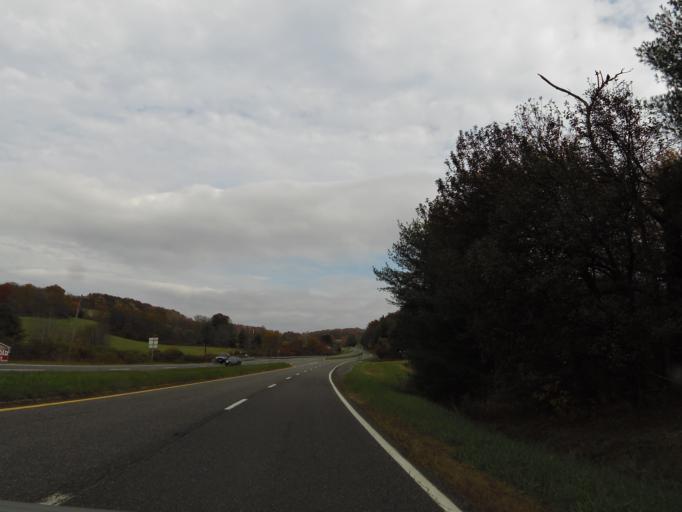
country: US
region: Virginia
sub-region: Carroll County
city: Hillsville
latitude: 36.6760
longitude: -80.7062
